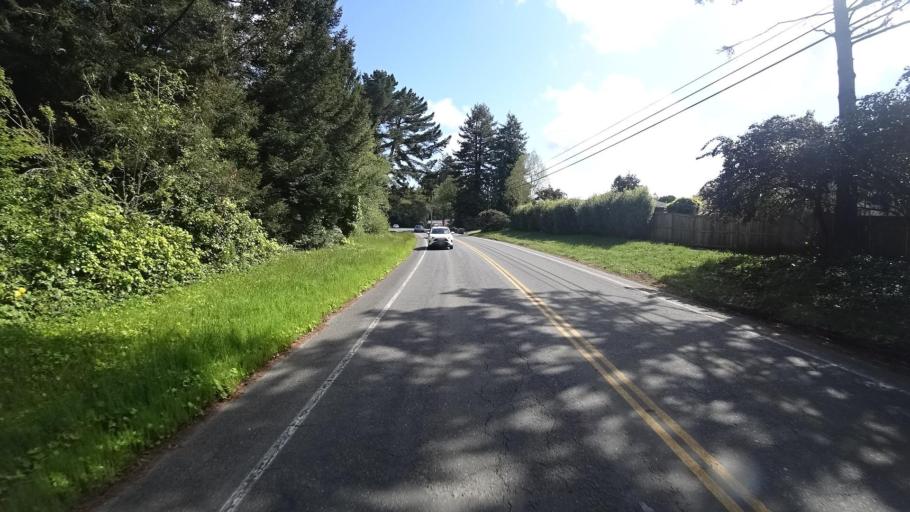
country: US
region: California
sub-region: Humboldt County
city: Pine Hills
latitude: 40.7339
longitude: -124.1505
